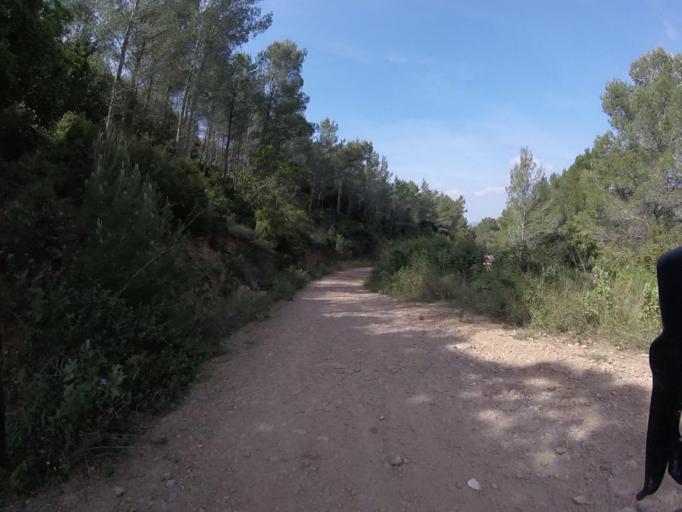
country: ES
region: Valencia
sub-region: Provincia de Castello
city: Benicassim
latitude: 40.0996
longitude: 0.0409
